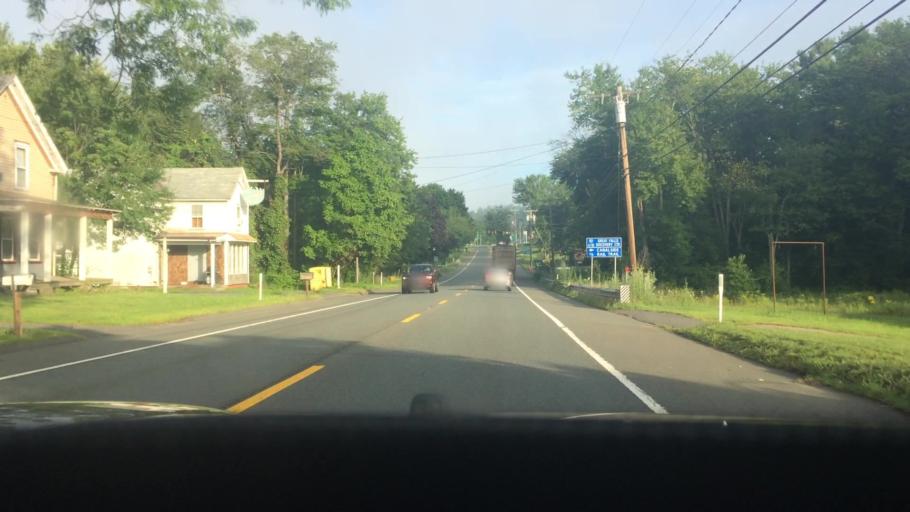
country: US
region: Massachusetts
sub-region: Franklin County
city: Turners Falls
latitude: 42.6110
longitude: -72.5444
